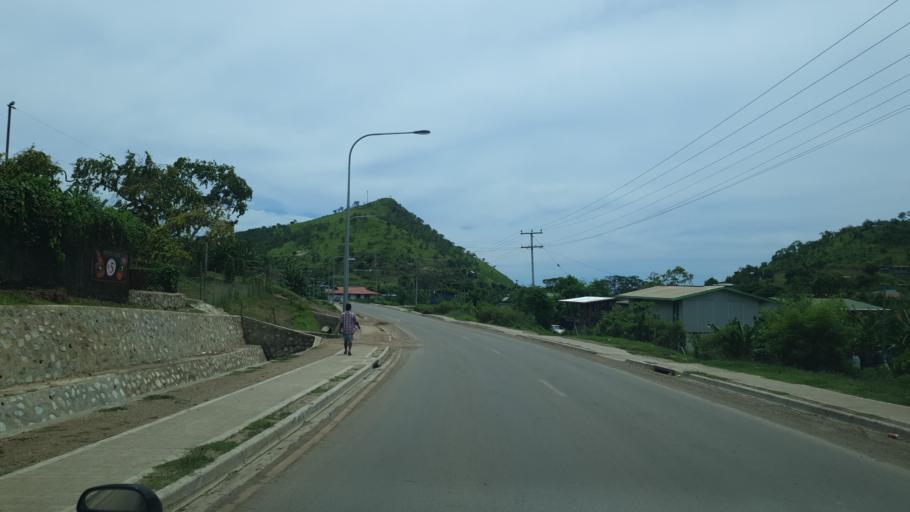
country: PG
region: National Capital
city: Port Moresby
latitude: -9.5231
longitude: 147.2409
